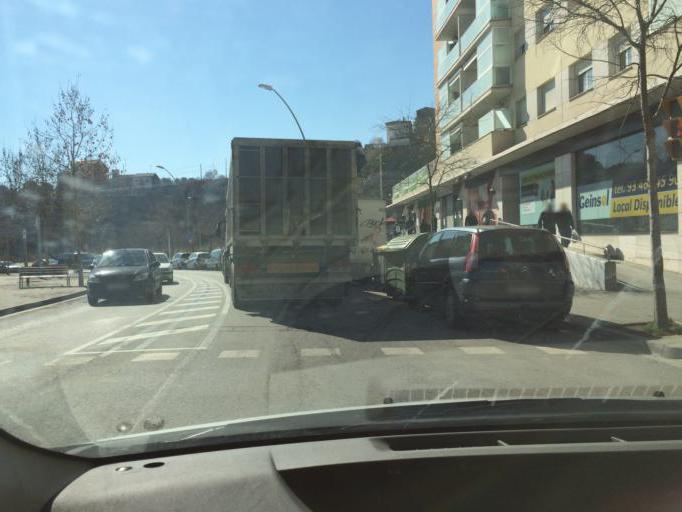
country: ES
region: Catalonia
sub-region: Provincia de Barcelona
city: Manresa
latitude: 41.7220
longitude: 1.8158
